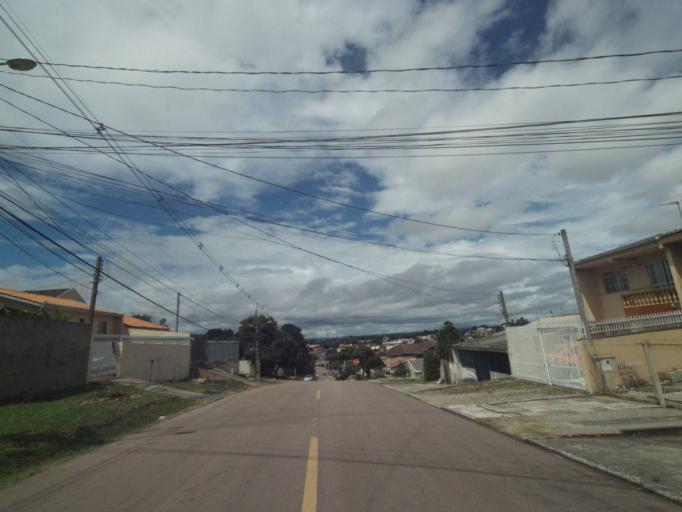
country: BR
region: Parana
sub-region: Curitiba
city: Curitiba
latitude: -25.4825
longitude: -49.2790
